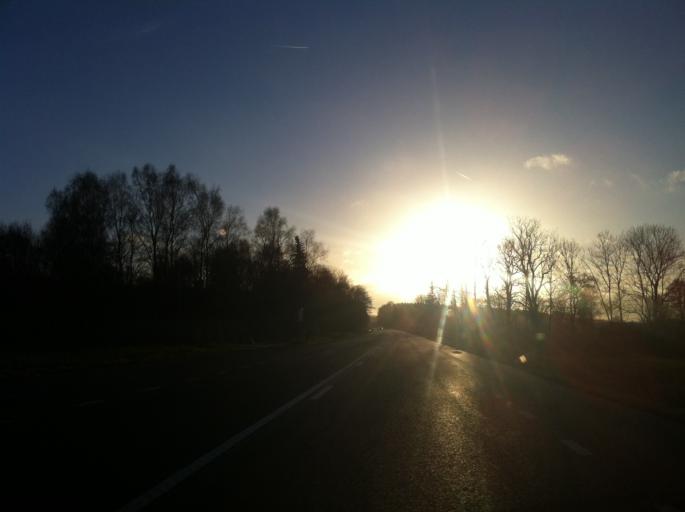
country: SE
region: Skane
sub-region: Hassleholms Kommun
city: Tormestorp
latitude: 56.0977
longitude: 13.7751
